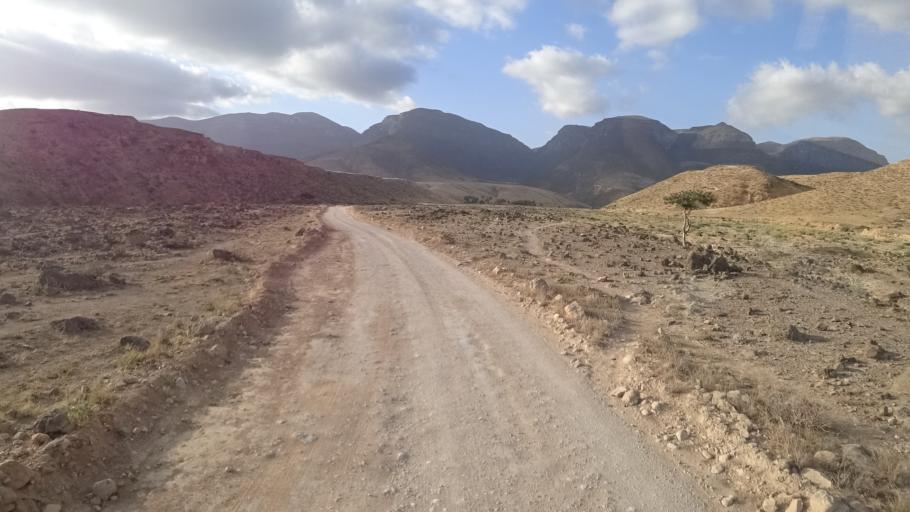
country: OM
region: Zufar
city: Salalah
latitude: 16.9813
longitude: 53.8520
